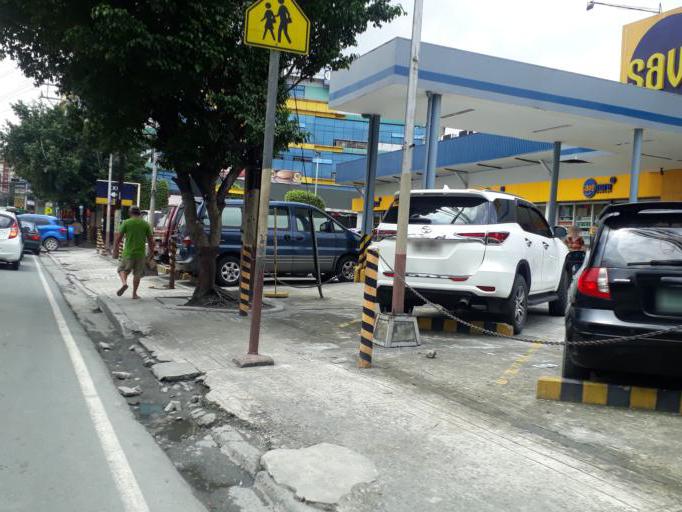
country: PH
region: Metro Manila
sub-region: Marikina
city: Calumpang
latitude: 14.6106
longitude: 121.0920
